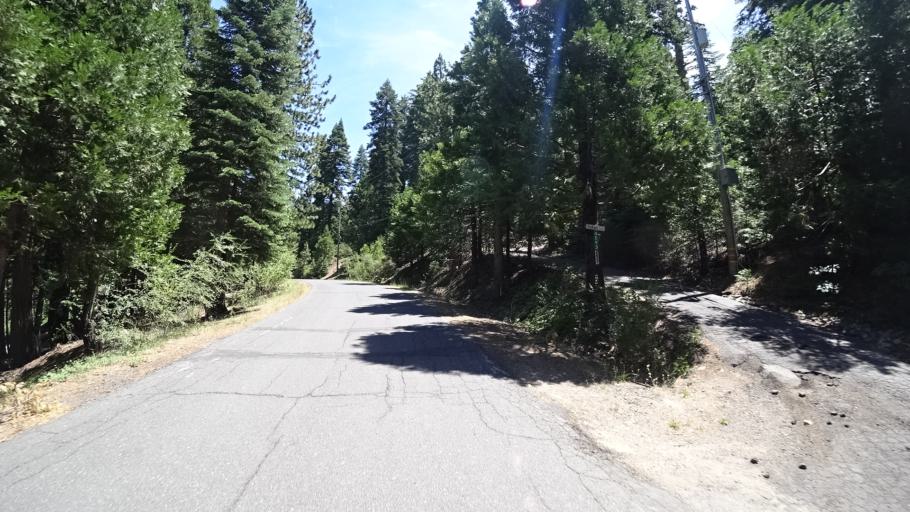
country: US
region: California
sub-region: Calaveras County
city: Arnold
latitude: 38.3163
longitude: -120.2560
